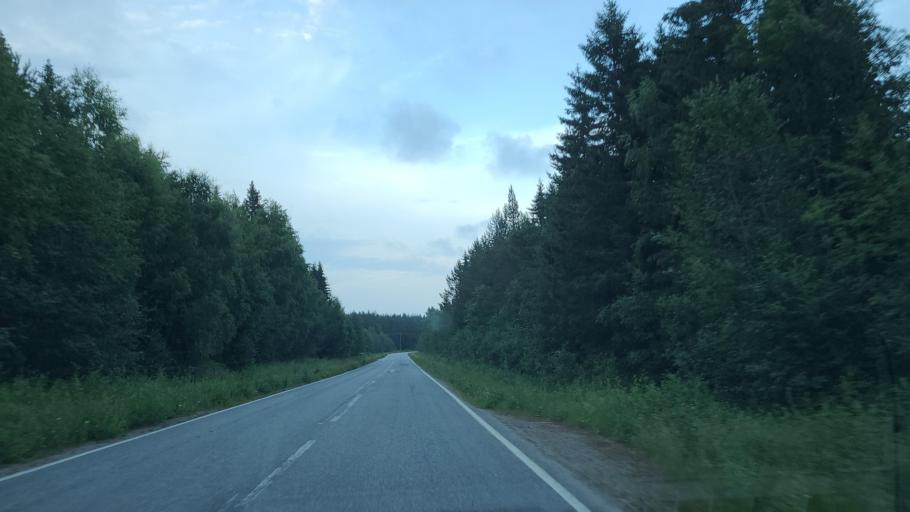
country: FI
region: Ostrobothnia
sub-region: Vaasa
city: Replot
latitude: 63.2728
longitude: 21.1605
